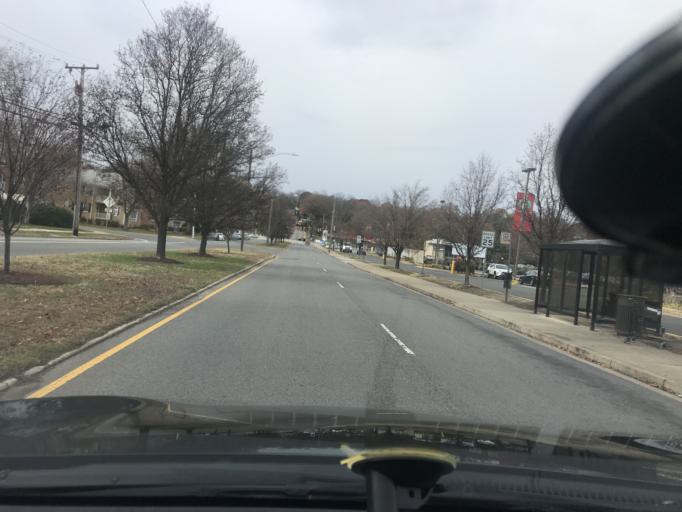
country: US
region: Virginia
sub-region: Fairfax County
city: Belle Haven
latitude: 38.7751
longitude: -77.0598
